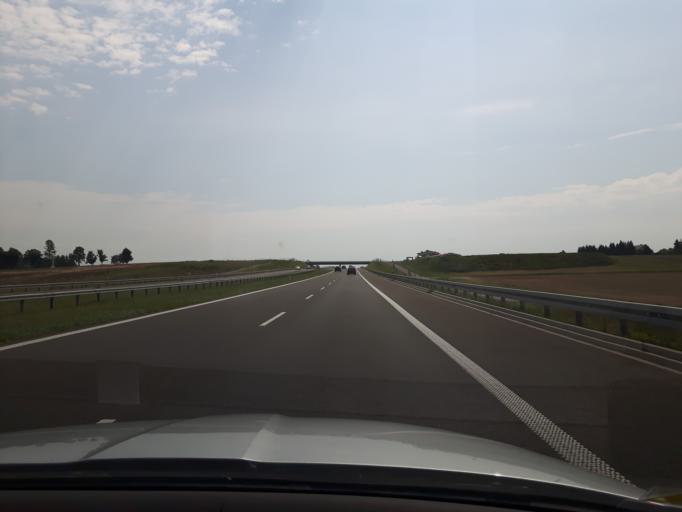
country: PL
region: Warmian-Masurian Voivodeship
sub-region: Powiat nidzicki
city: Nidzica
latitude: 53.3601
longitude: 20.3899
